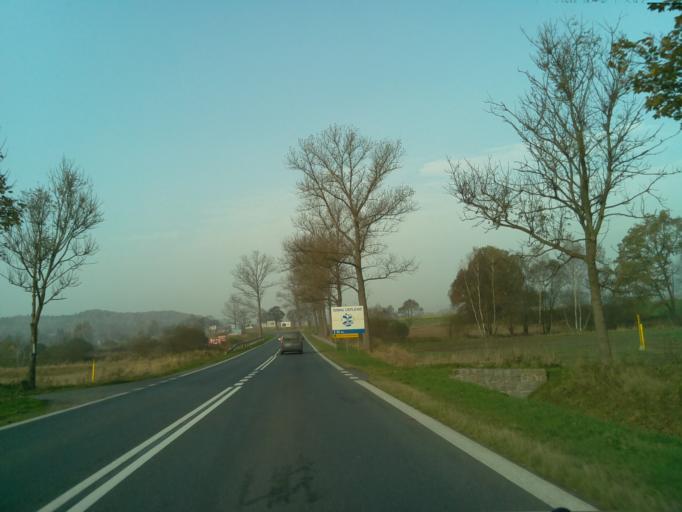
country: PL
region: Lower Silesian Voivodeship
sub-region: Powiat jeleniogorski
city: Janowice Wielkie
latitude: 50.9067
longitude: 15.8545
